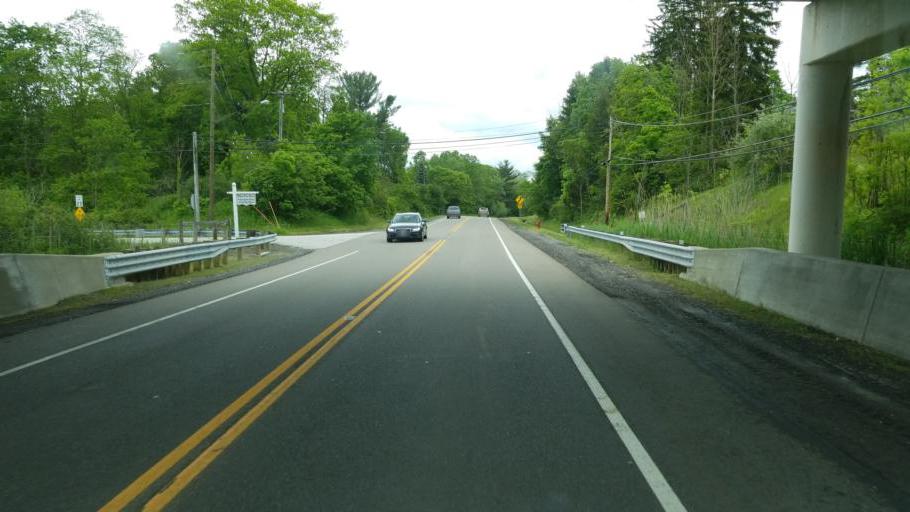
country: US
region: Ohio
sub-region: Summit County
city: Richfield
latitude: 41.2398
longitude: -81.6284
